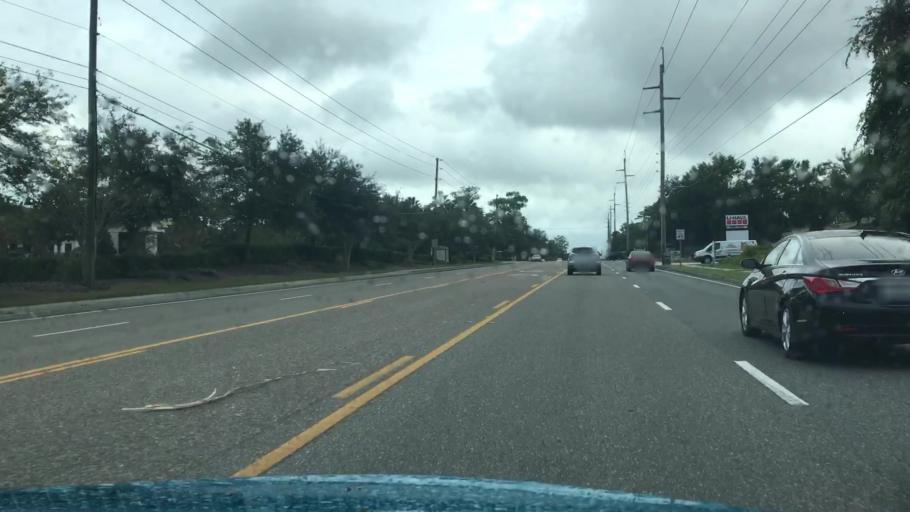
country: US
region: Florida
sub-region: Volusia County
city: Deltona
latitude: 28.9002
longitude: -81.2861
